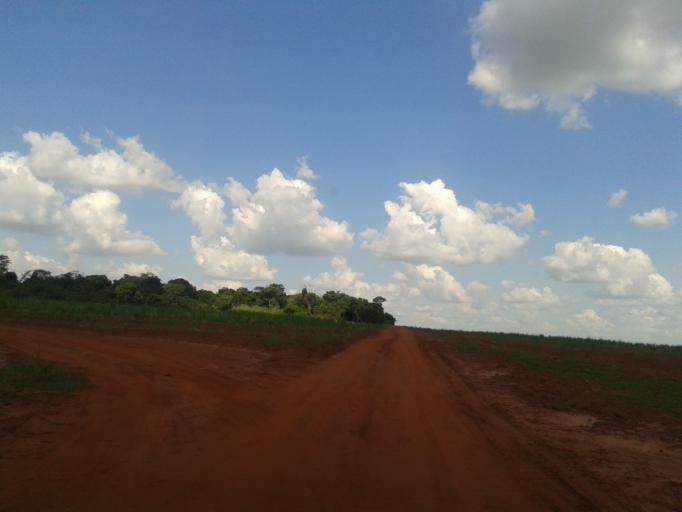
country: BR
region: Minas Gerais
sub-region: Ituiutaba
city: Ituiutaba
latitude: -19.1812
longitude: -49.7233
